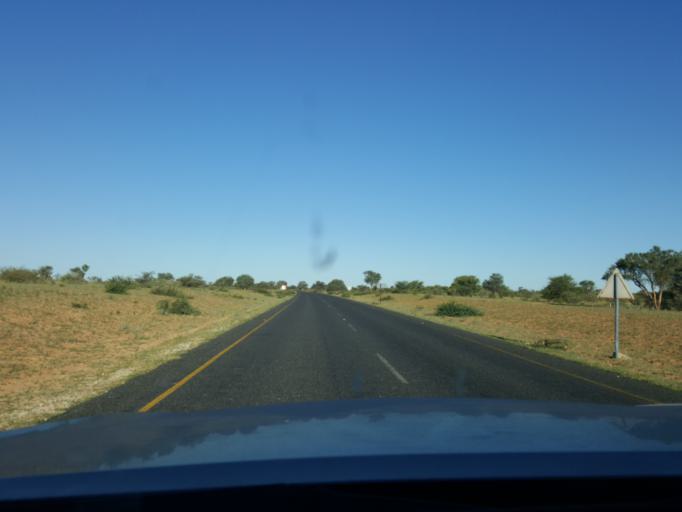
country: BW
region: Southern
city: Khakhea
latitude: -24.2307
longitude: 23.2475
